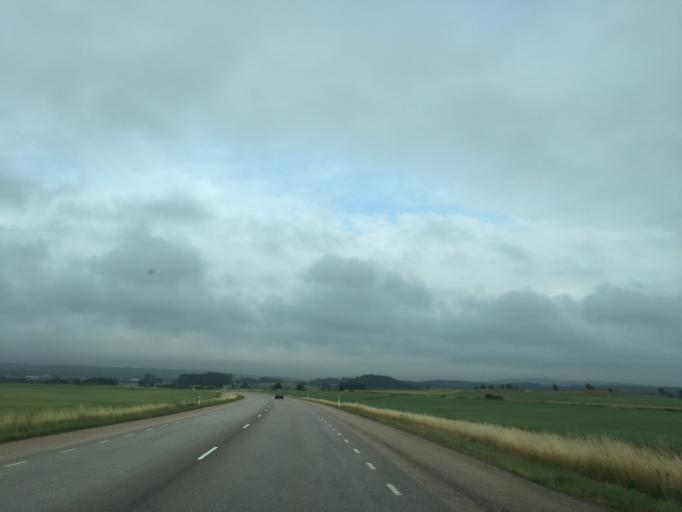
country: SE
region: Halland
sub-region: Falkenbergs Kommun
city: Falkenberg
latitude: 56.8834
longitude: 12.5749
